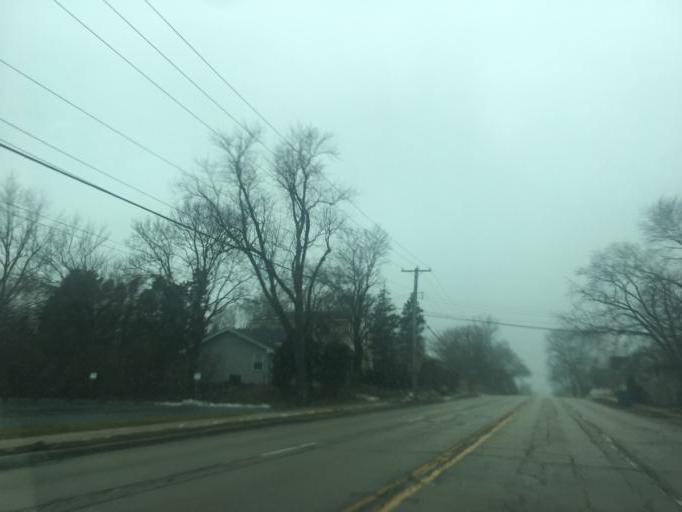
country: US
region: Illinois
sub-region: DuPage County
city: Downers Grove
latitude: 41.7878
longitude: -88.0005
